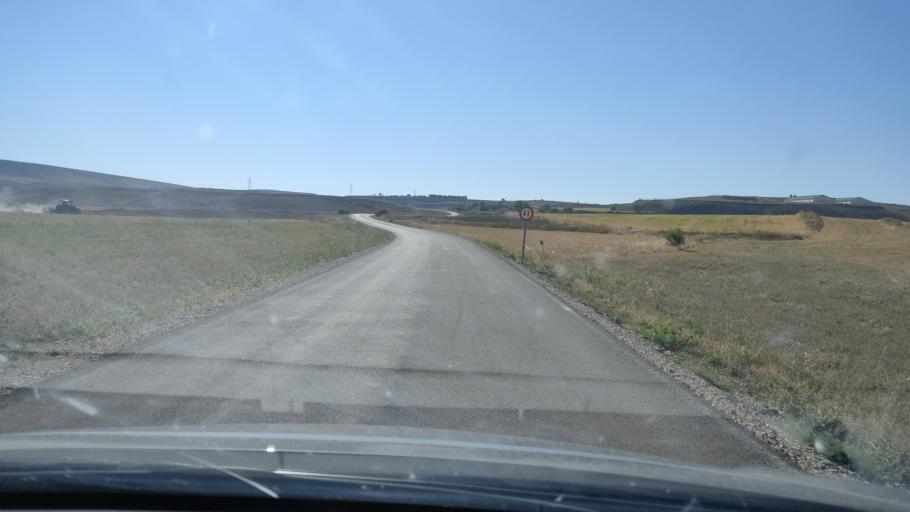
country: ES
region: Aragon
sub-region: Provincia de Teruel
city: Monforte de Moyuela
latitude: 41.0453
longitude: -1.0018
